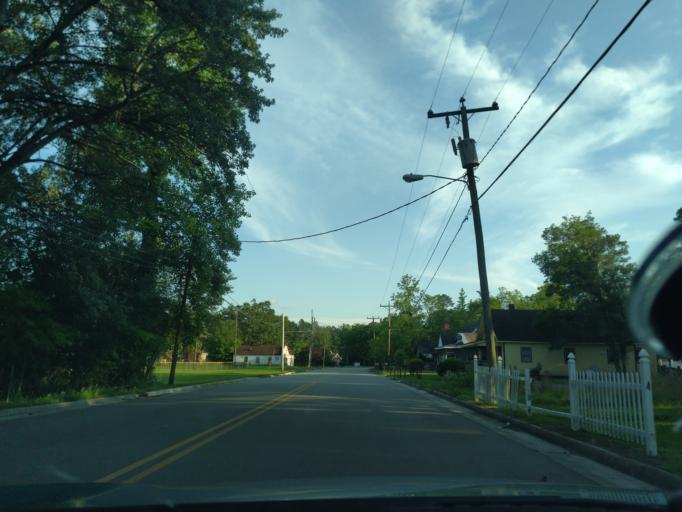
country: US
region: North Carolina
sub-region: Washington County
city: Plymouth
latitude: 35.8587
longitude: -76.7540
